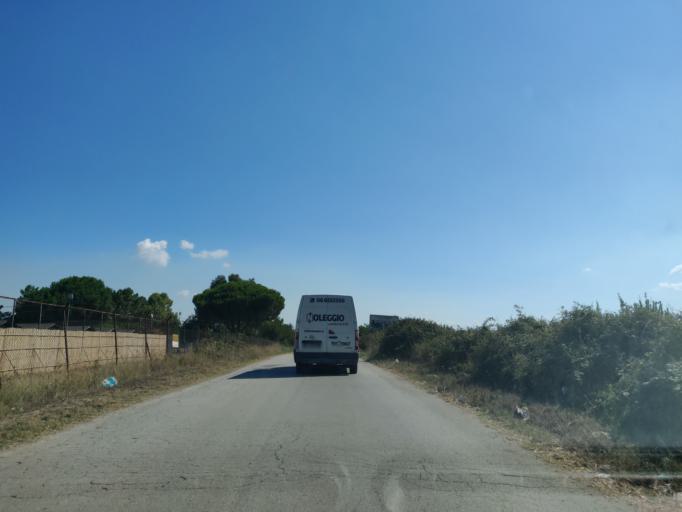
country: IT
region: Latium
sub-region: Citta metropolitana di Roma Capitale
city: Aurelia
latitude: 42.1659
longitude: 11.7419
